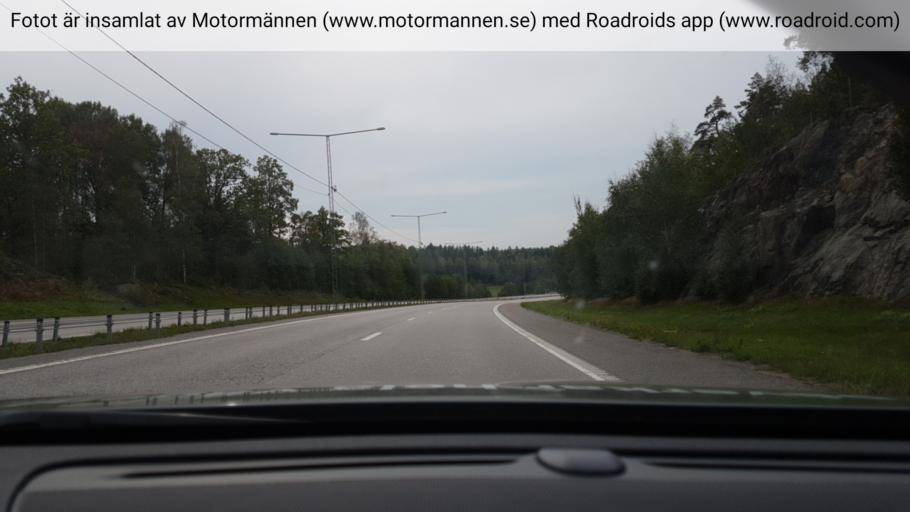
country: SE
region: Stockholm
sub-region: Haninge Kommun
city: Haninge
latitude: 59.1390
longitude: 18.1607
